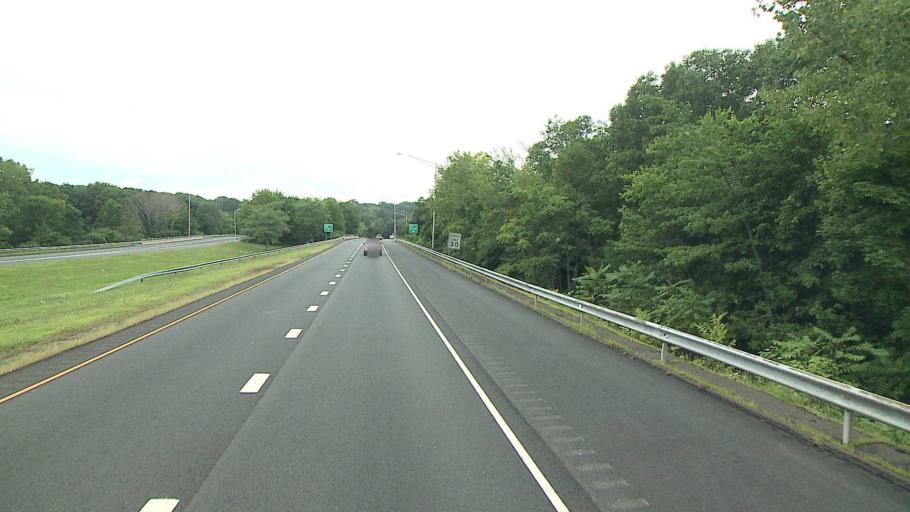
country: US
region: Connecticut
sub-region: New Haven County
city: Hamden
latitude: 41.3997
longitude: -72.8941
